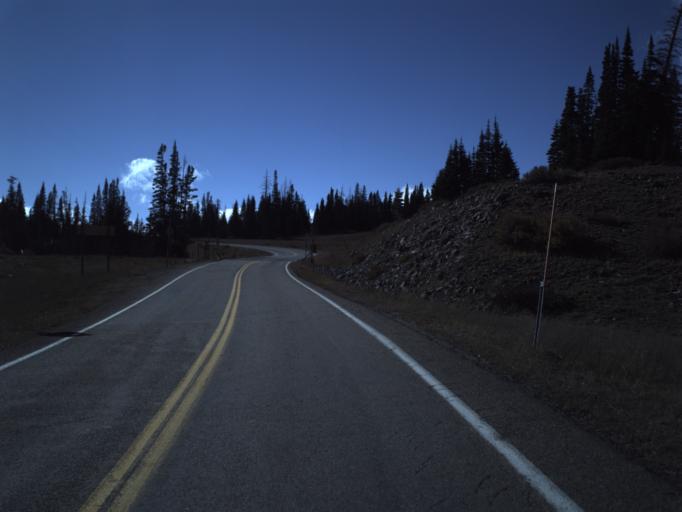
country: US
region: Utah
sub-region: Iron County
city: Parowan
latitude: 37.6560
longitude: -112.8186
